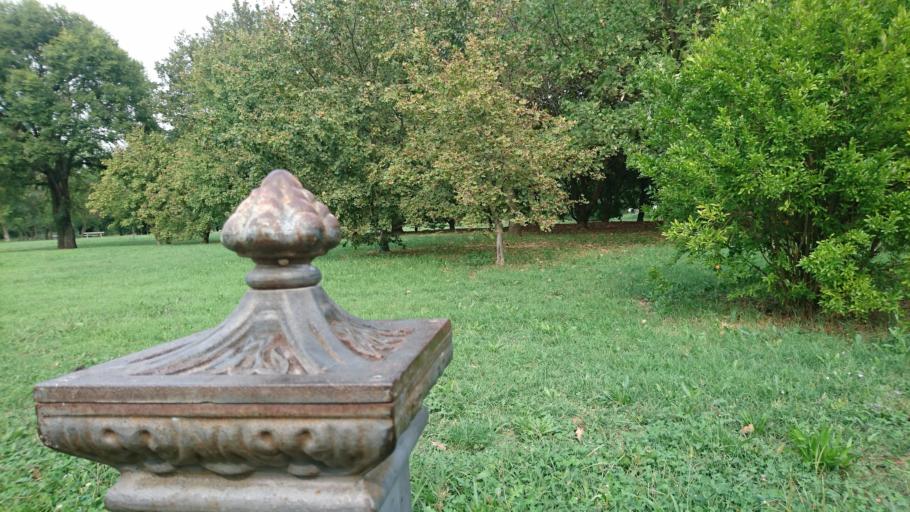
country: IT
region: Veneto
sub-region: Provincia di Padova
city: Villaguattera
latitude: 45.4361
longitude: 11.8459
